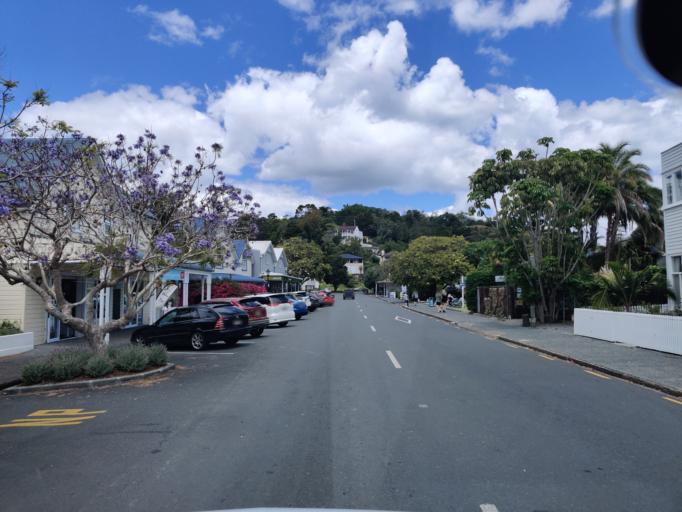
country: NZ
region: Northland
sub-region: Far North District
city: Paihia
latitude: -35.2621
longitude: 174.1223
